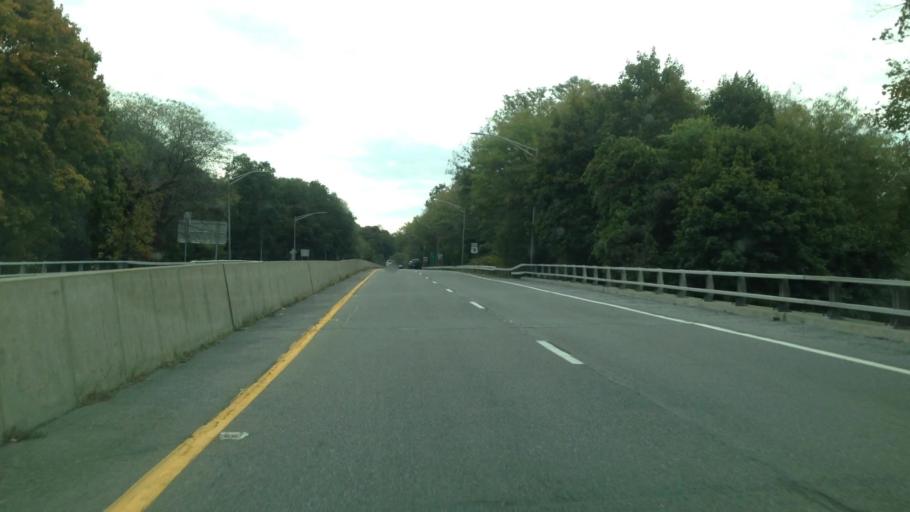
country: US
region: New York
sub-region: Dutchess County
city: Poughkeepsie
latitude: 41.6911
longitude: -73.9363
